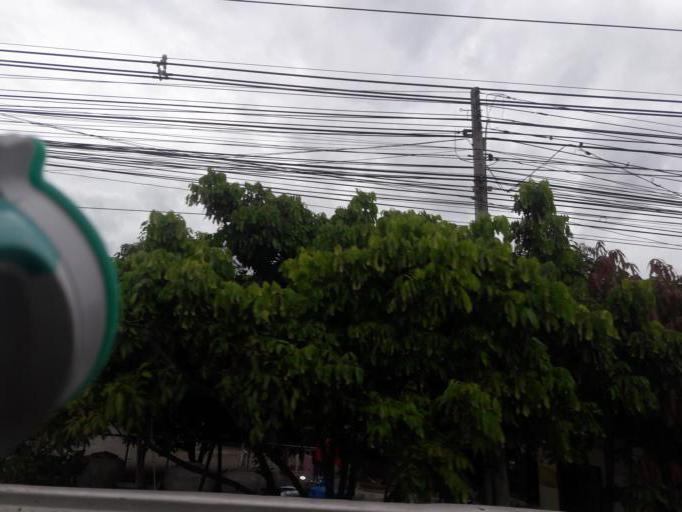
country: TH
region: Ratchaburi
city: Damnoen Saduak
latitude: 13.5171
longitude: 99.9725
